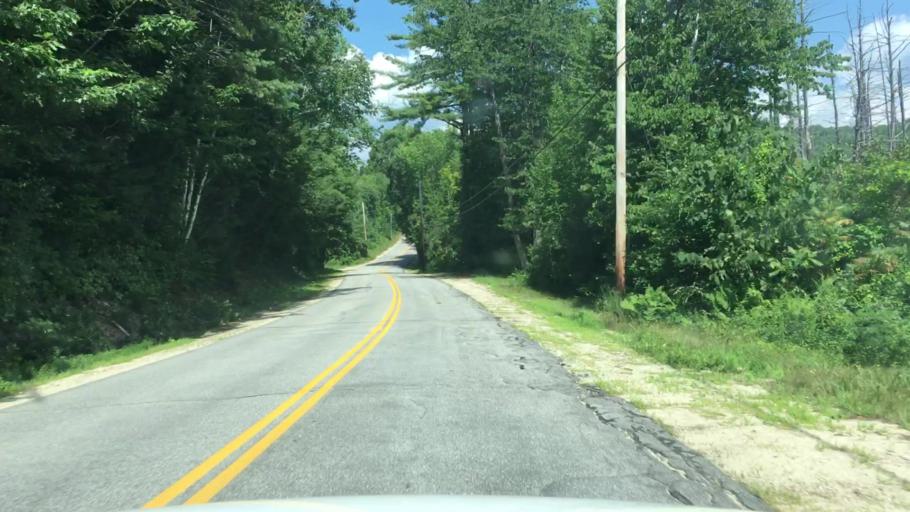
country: US
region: Maine
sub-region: Cumberland County
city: Raymond
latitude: 43.9353
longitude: -70.5210
